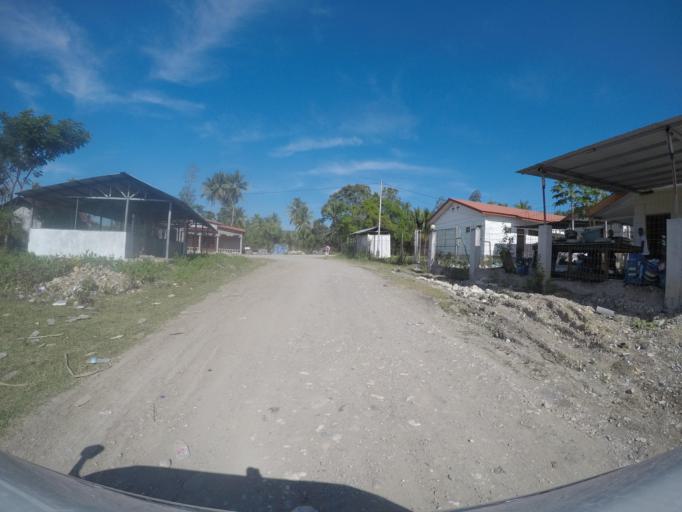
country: TL
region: Viqueque
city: Viqueque
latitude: -8.8515
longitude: 126.3609
